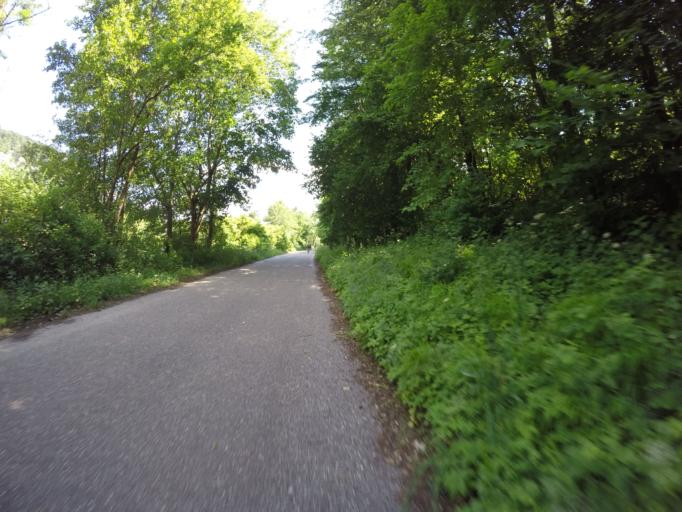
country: DE
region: Bavaria
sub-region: Lower Bavaria
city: Essing
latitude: 48.9347
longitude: 11.7864
